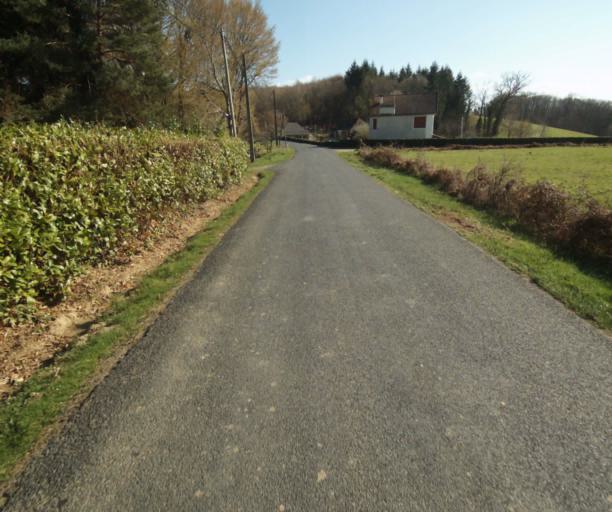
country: FR
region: Limousin
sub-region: Departement de la Correze
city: Saint-Mexant
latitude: 45.3077
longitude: 1.6152
